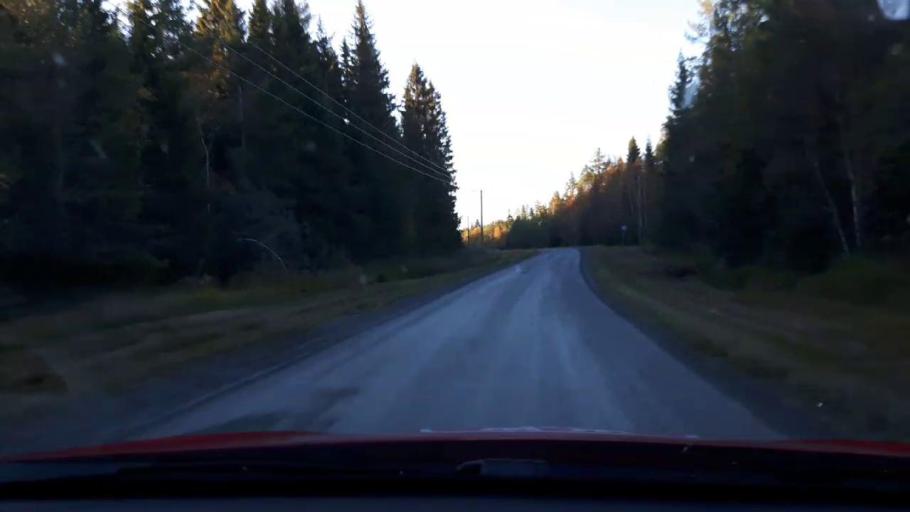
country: SE
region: Jaemtland
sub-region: Krokoms Kommun
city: Krokom
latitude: 63.4480
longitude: 14.4181
